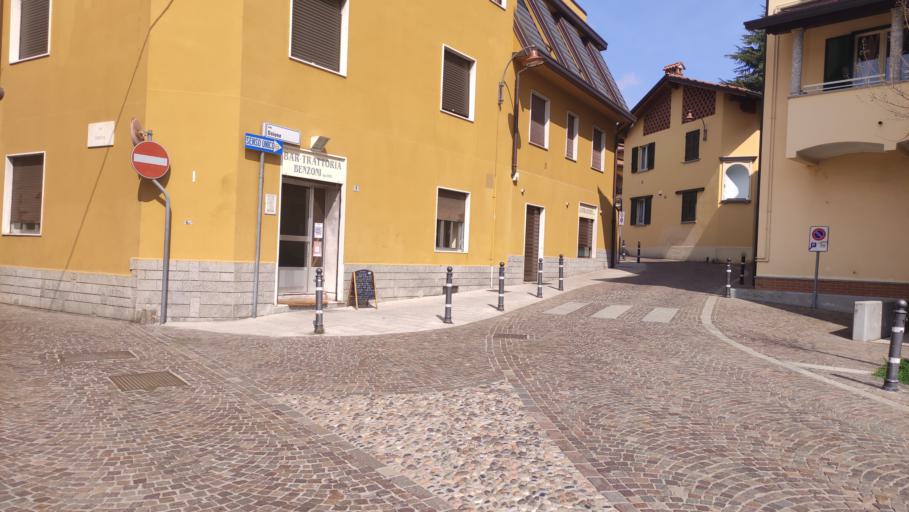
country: IT
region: Lombardy
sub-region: Provincia di Como
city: Cermenate
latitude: 45.7030
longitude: 9.0947
